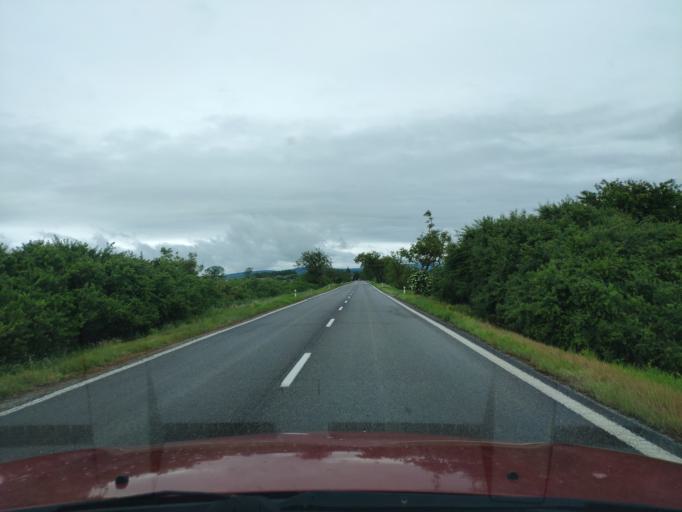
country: HU
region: Borsod-Abauj-Zemplen
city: Karcsa
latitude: 48.4339
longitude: 21.8776
